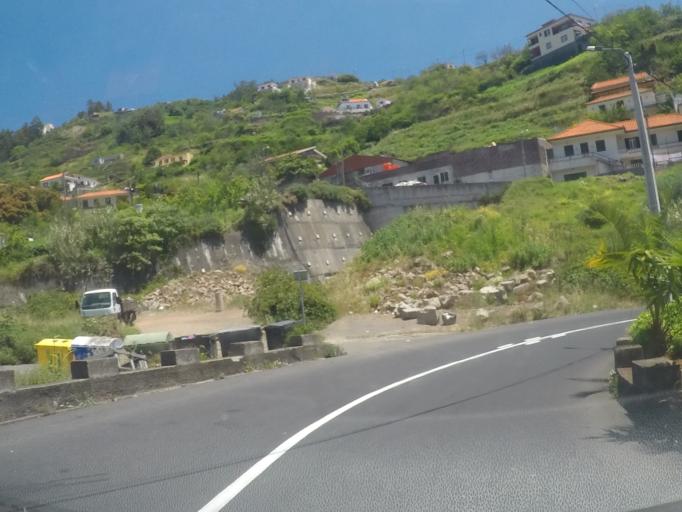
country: PT
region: Madeira
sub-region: Camara de Lobos
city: Curral das Freiras
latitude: 32.6882
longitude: -16.9940
